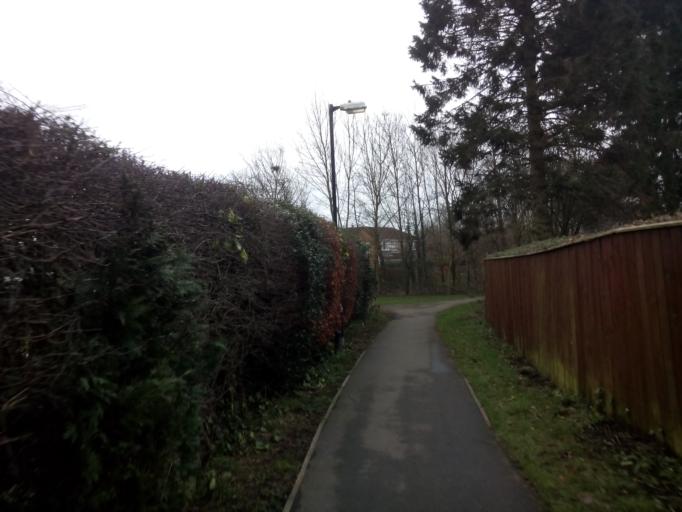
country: GB
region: England
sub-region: County Durham
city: Chester-le-Street
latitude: 54.8483
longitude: -1.5653
